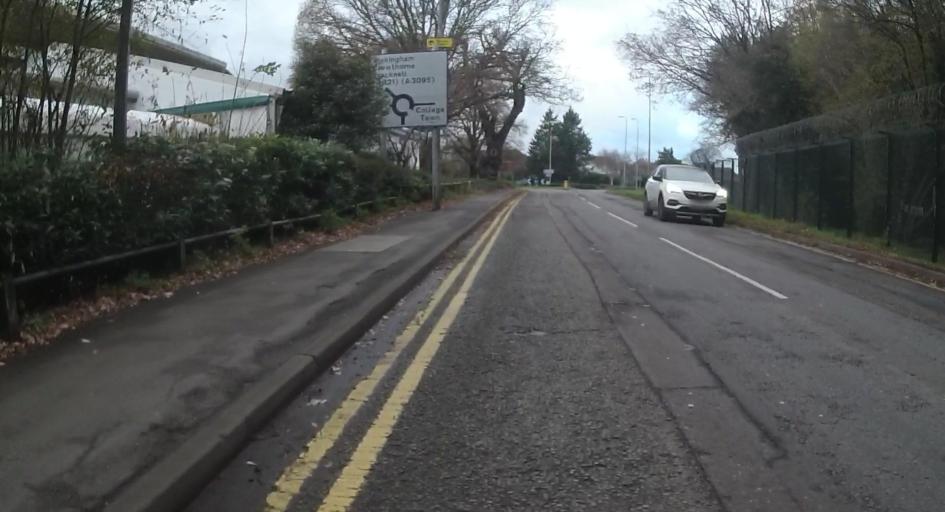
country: GB
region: England
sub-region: Bracknell Forest
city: Sandhurst
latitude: 51.3370
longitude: -0.7751
